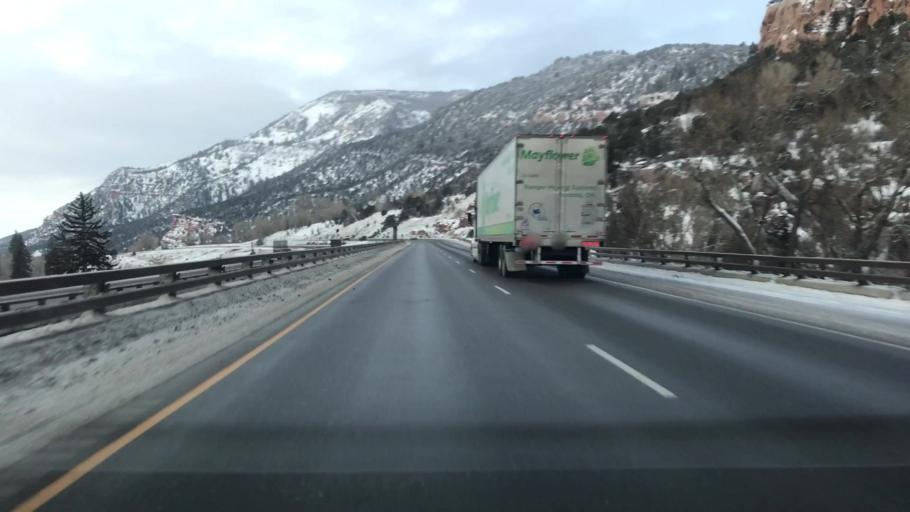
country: US
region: Colorado
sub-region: Eagle County
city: Eagle
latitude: 39.7110
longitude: -106.7102
